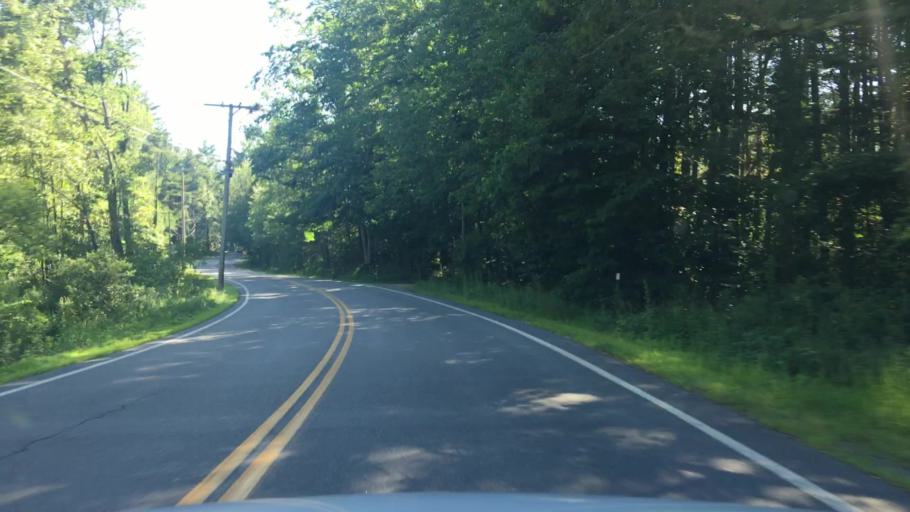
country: US
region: New Hampshire
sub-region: Rockingham County
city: Brentwood
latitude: 42.9886
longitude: -71.0535
